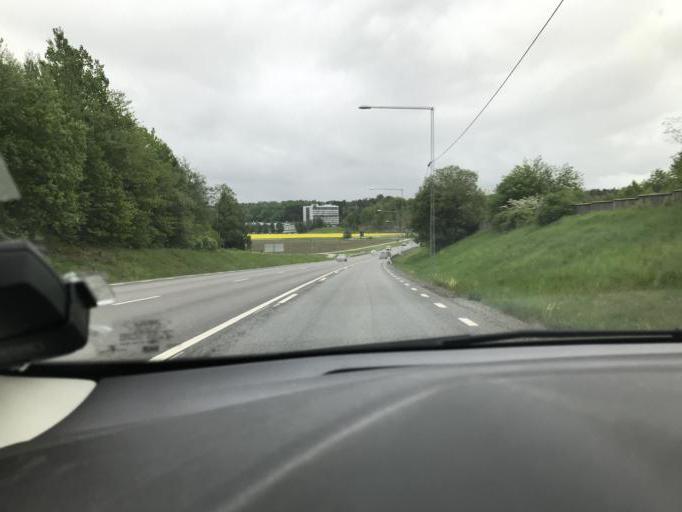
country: SE
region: Stockholm
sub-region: Botkyrka Kommun
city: Tumba
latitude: 59.2074
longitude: 17.8383
